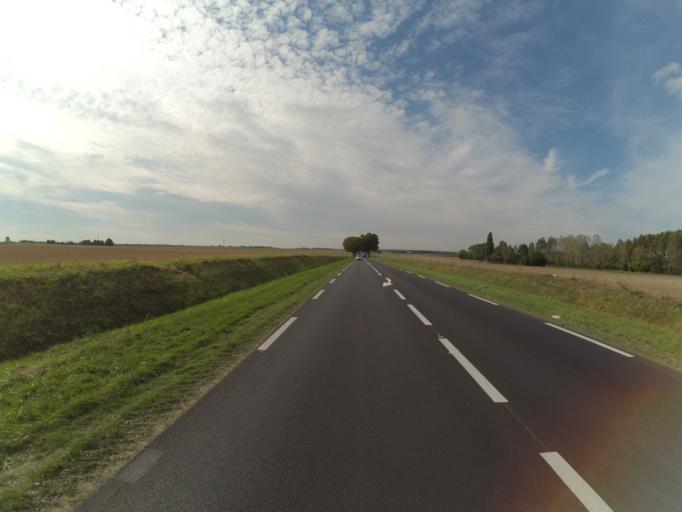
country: FR
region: Pays de la Loire
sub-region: Departement de Maine-et-Loire
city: Distre
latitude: 47.2237
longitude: -0.1466
